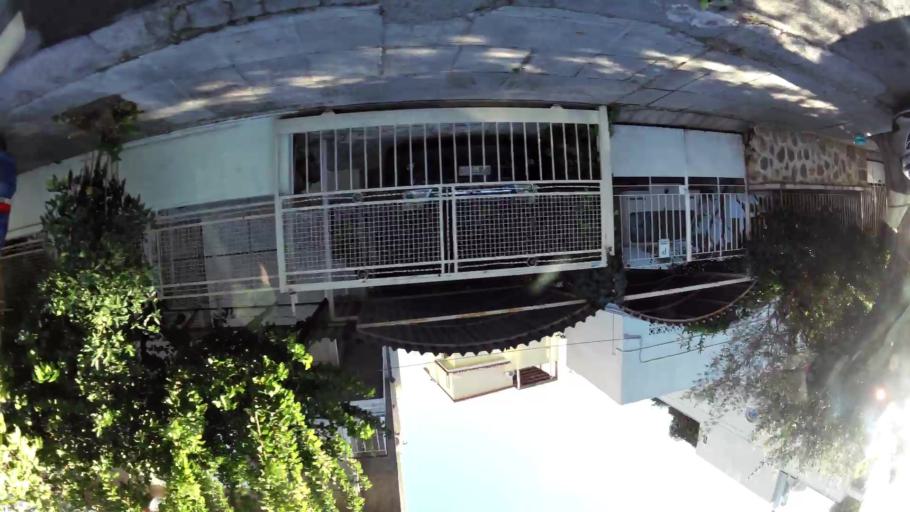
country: GR
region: Attica
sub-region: Nomarchia Athinas
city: Khalandrion
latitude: 38.0172
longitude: 23.7912
